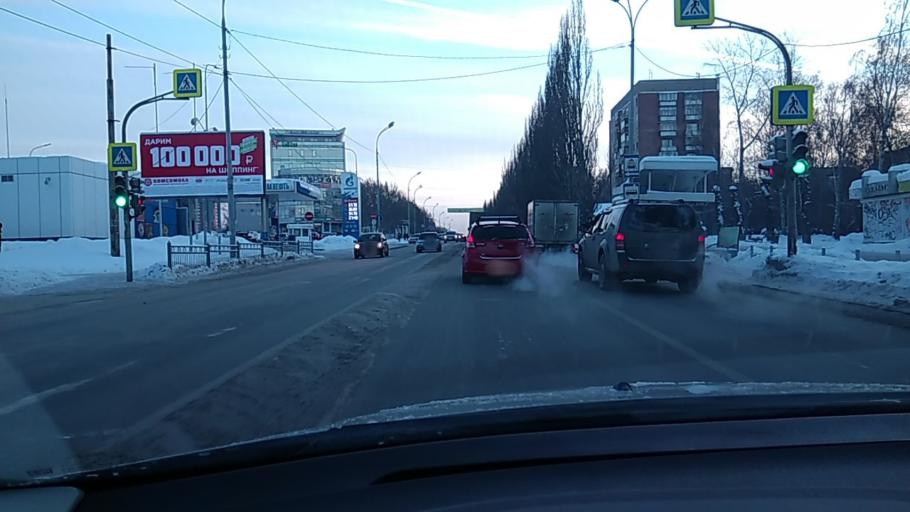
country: RU
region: Sverdlovsk
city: Yekaterinburg
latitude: 56.8356
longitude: 60.6341
